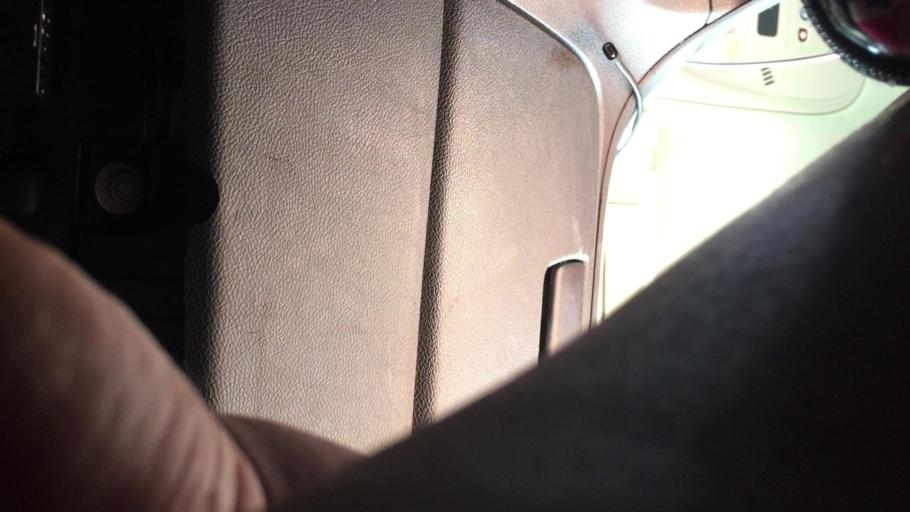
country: US
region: Georgia
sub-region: Carroll County
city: Carrollton
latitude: 33.5993
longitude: -85.0312
